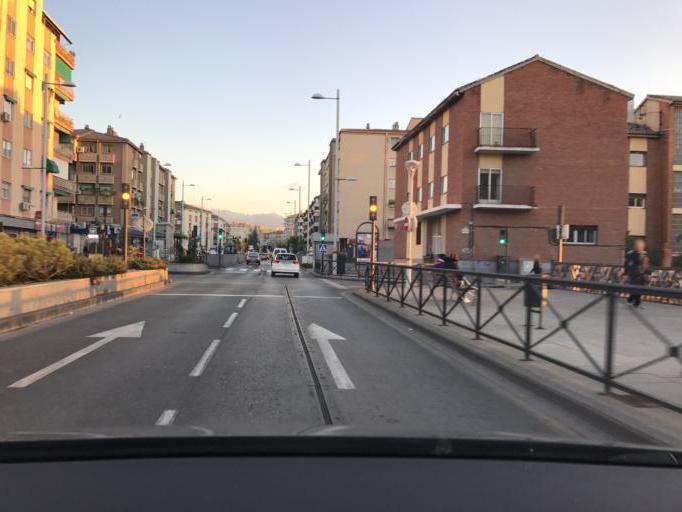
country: ES
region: Andalusia
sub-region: Provincia de Granada
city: Granada
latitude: 37.1659
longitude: -3.6033
